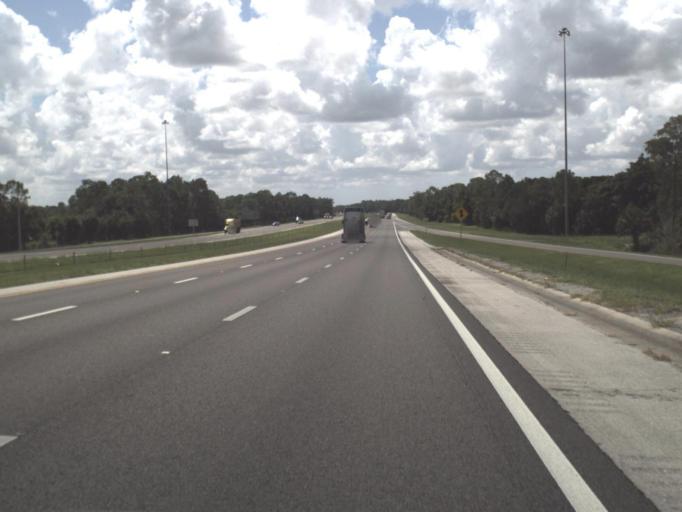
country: US
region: Florida
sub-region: Lee County
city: Bonita Springs
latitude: 26.3295
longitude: -81.7499
